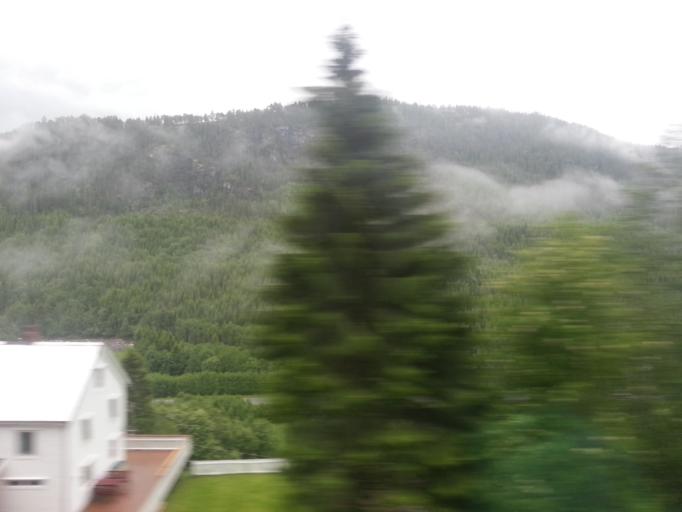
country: NO
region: Sor-Trondelag
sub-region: Midtre Gauldal
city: Storen
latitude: 63.0100
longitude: 10.2397
